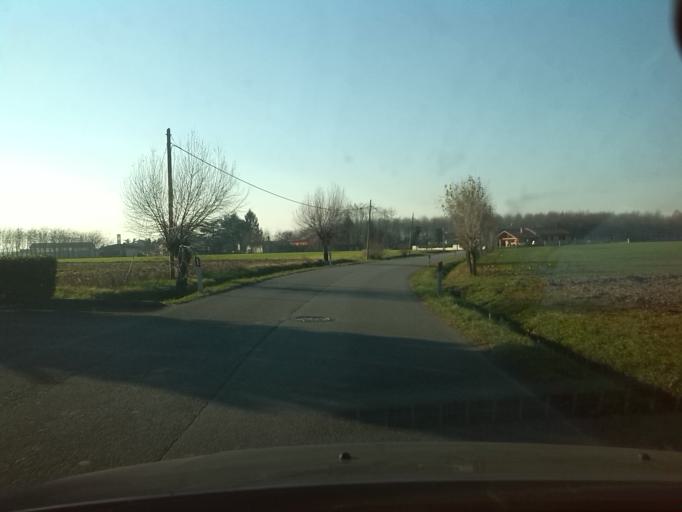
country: IT
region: Friuli Venezia Giulia
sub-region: Provincia di Udine
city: Percoto
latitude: 45.9523
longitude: 13.3166
